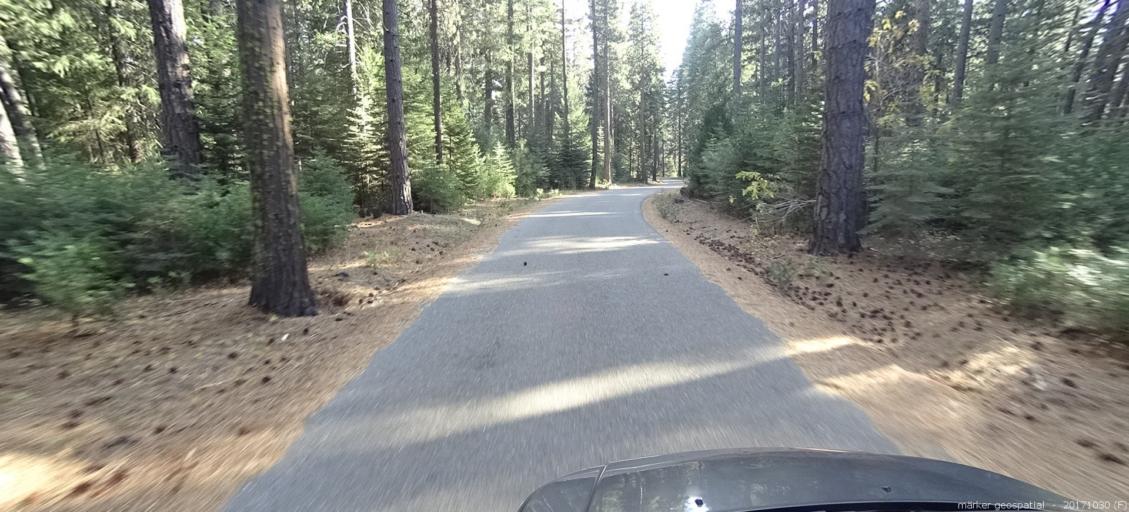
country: US
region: California
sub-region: Shasta County
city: Shingletown
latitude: 40.5218
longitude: -121.6883
